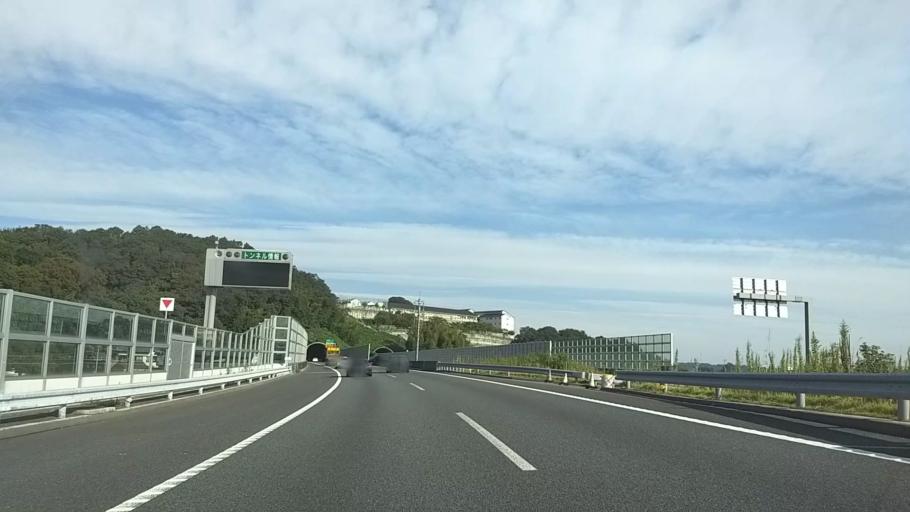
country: JP
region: Kanagawa
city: Zama
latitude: 35.5072
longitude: 139.3659
